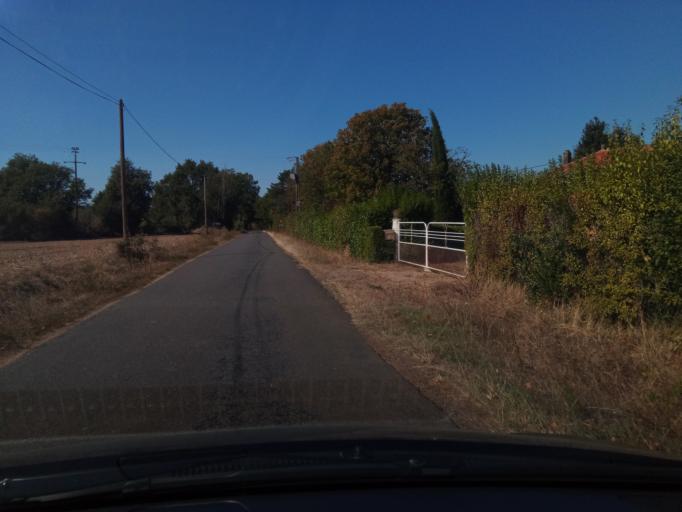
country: FR
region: Poitou-Charentes
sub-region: Departement de la Vienne
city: Montmorillon
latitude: 46.4821
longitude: 0.8505
